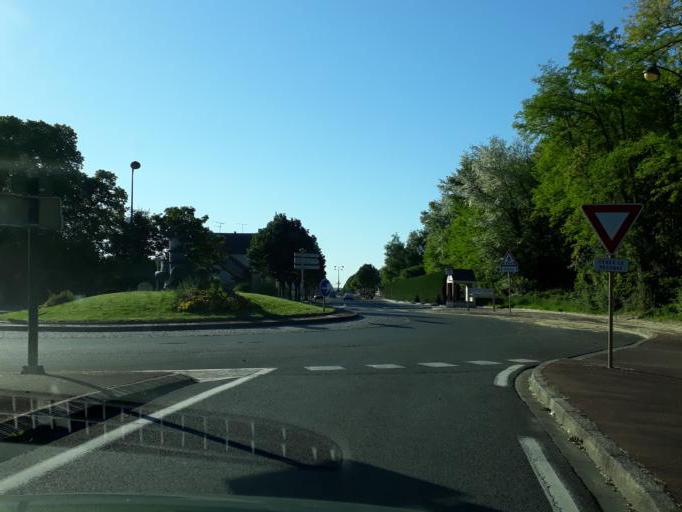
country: FR
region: Centre
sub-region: Departement du Loiret
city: Briare
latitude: 47.6307
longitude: 2.7481
